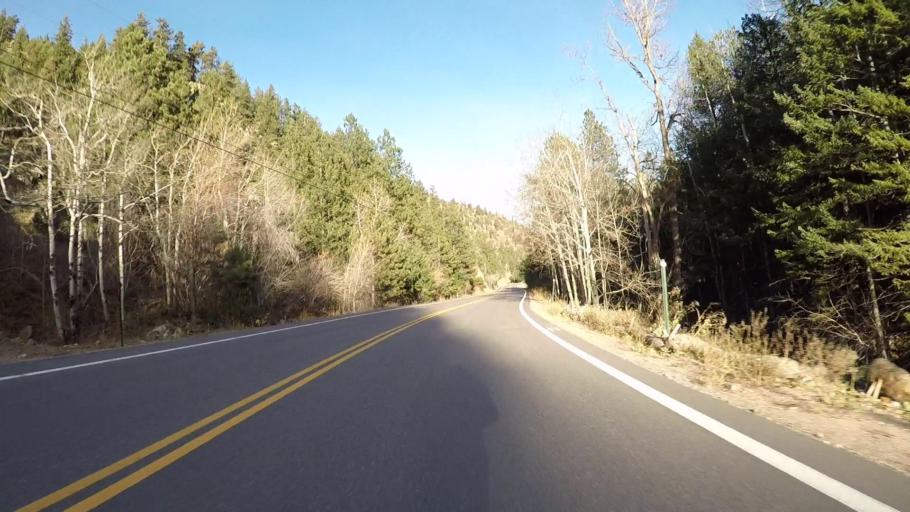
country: US
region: Colorado
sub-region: Boulder County
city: Boulder
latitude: 40.0758
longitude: -105.3971
